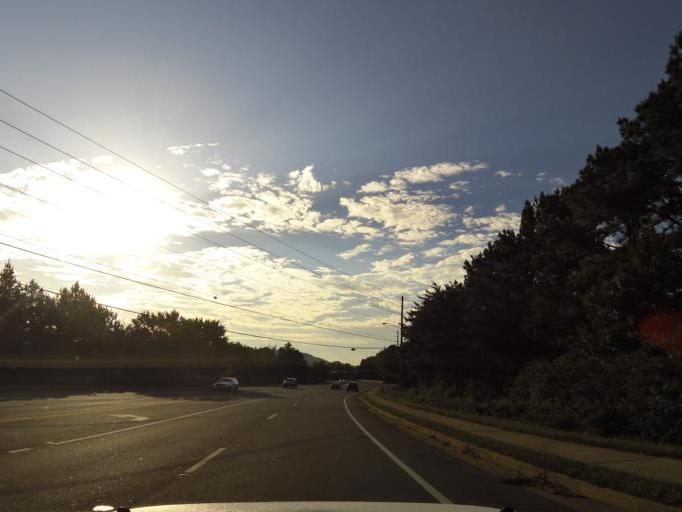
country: US
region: Georgia
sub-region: Cobb County
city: Kennesaw
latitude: 33.9885
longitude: -84.6249
